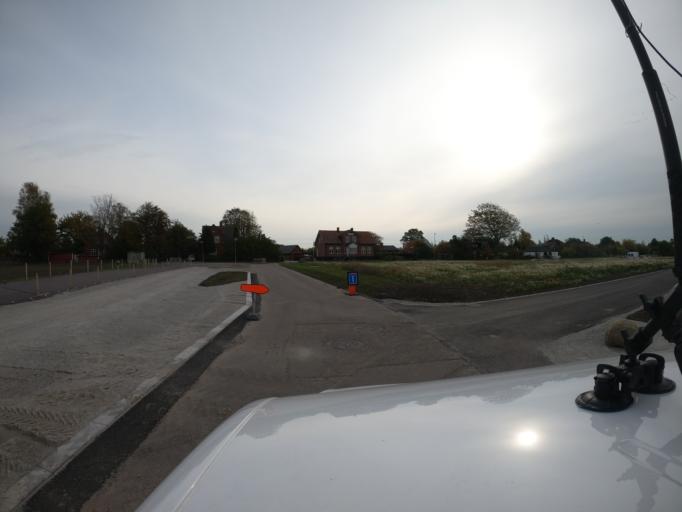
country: SE
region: Skane
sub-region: Lunds Kommun
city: Lund
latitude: 55.7551
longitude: 13.2004
